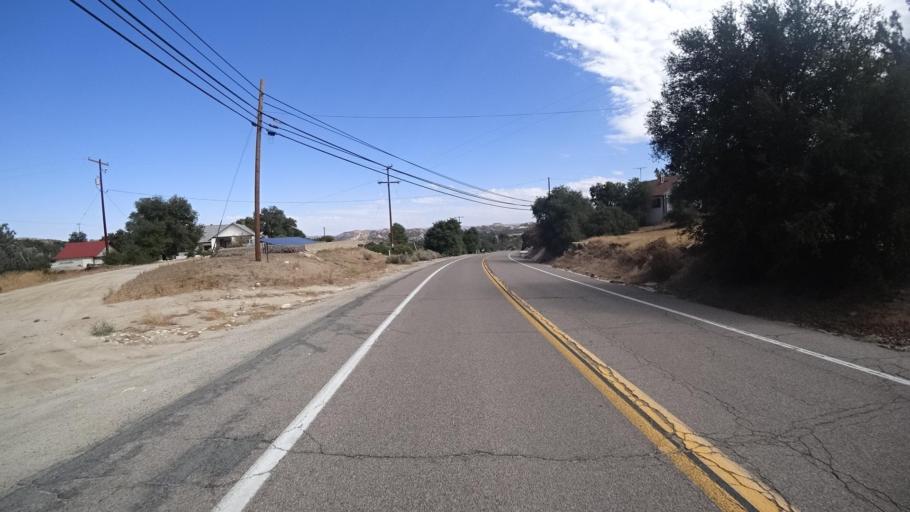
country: MX
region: Baja California
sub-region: Tecate
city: Cereso del Hongo
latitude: 32.6682
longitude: -116.2867
